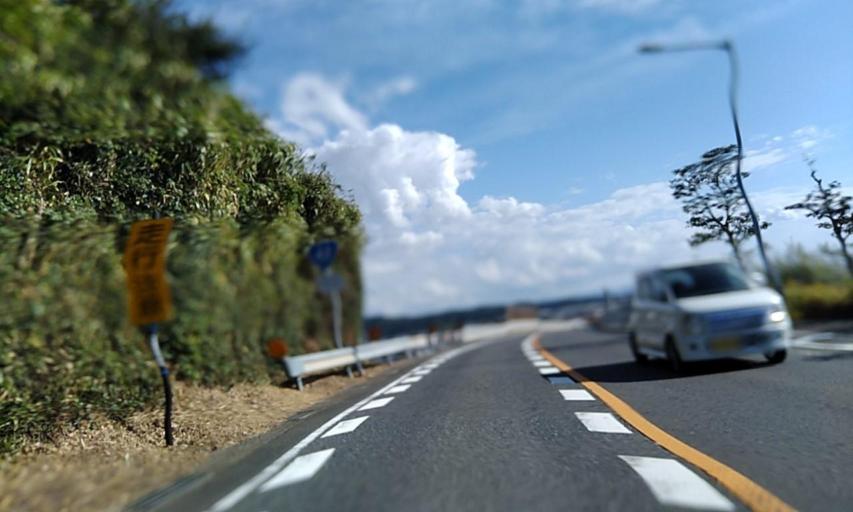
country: JP
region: Wakayama
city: Tanabe
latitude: 33.7763
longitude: 135.3107
